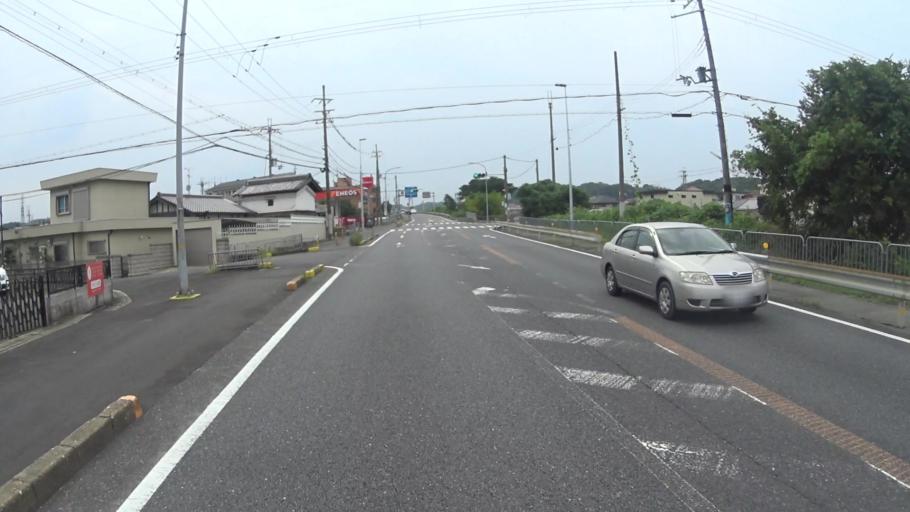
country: JP
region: Nara
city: Nara-shi
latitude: 34.7369
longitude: 135.7976
